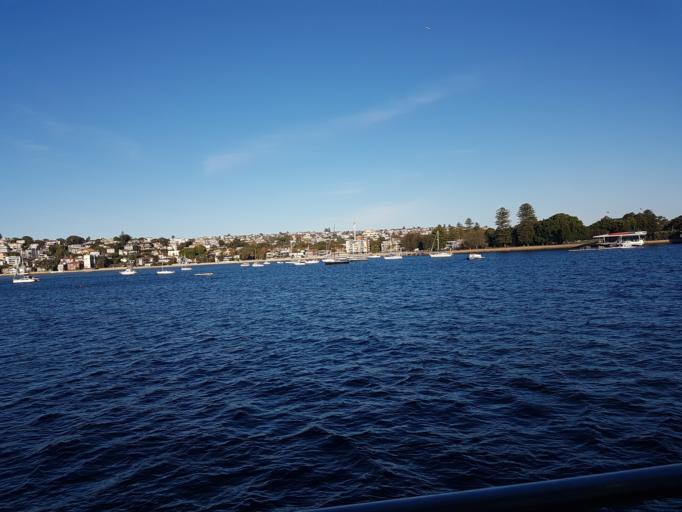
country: AU
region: New South Wales
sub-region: Woollahra
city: Point Piper
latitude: -33.8679
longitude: 151.2610
